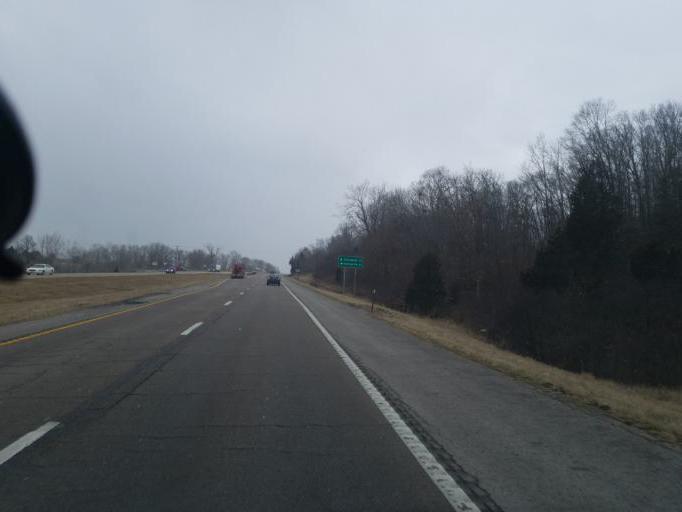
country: US
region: Missouri
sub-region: Boone County
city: Hallsville
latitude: 39.1217
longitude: -92.3315
